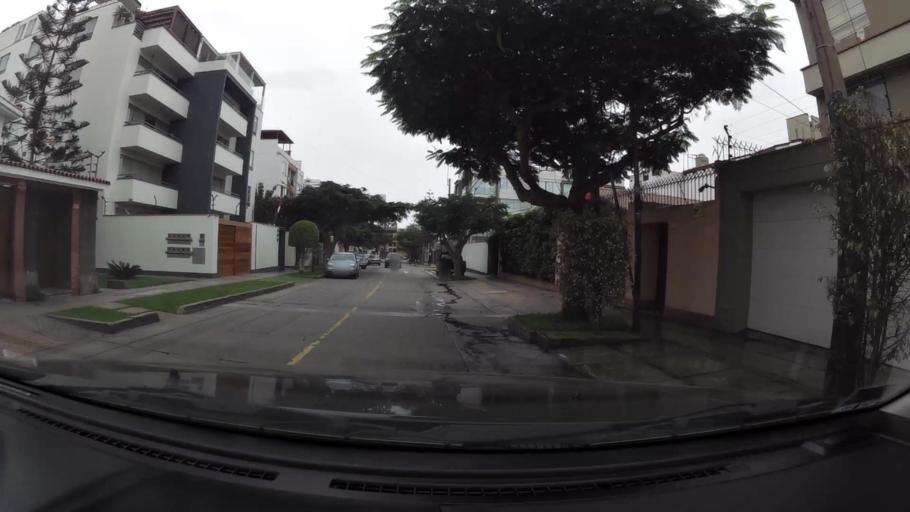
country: PE
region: Lima
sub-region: Lima
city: Surco
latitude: -12.1167
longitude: -76.9924
